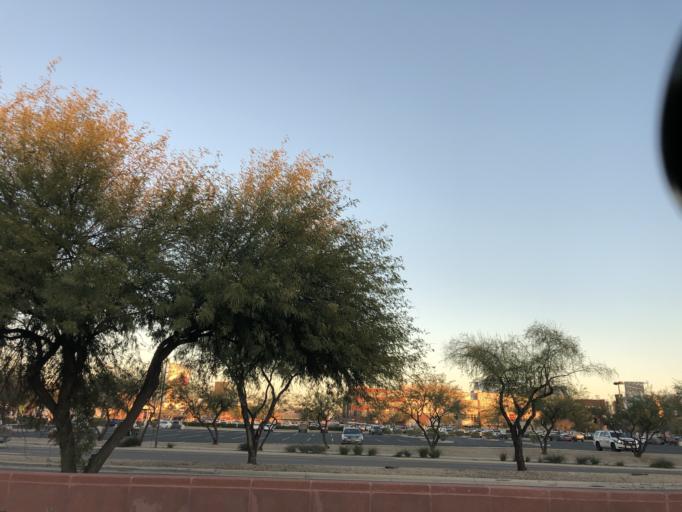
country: US
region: Arizona
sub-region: Maricopa County
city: Peoria
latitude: 33.5343
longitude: -112.2652
